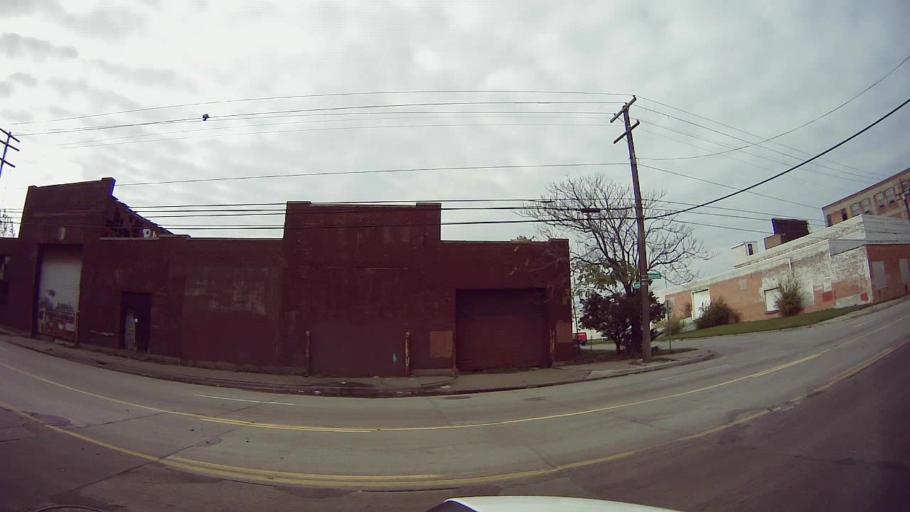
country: US
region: Michigan
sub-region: Wayne County
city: Hamtramck
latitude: 42.3684
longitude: -83.0549
